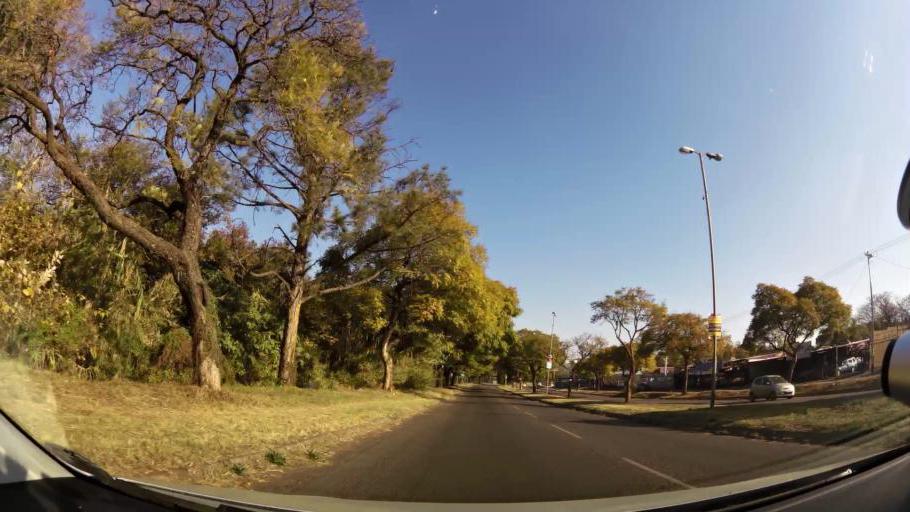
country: ZA
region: Gauteng
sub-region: City of Tshwane Metropolitan Municipality
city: Pretoria
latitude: -25.7562
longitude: 28.1426
